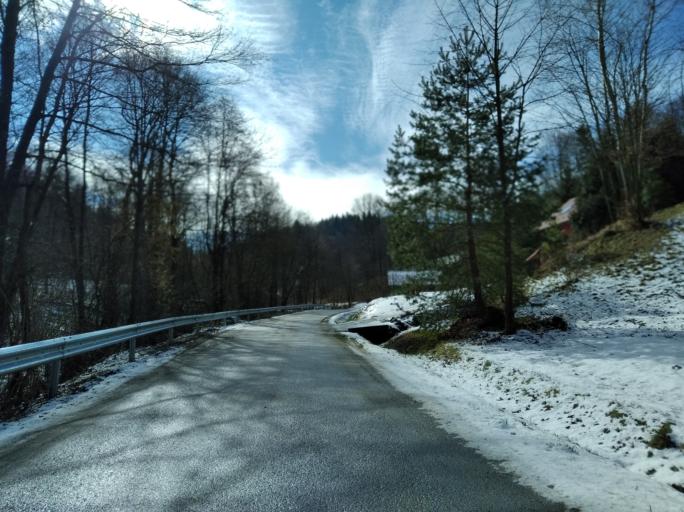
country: PL
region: Subcarpathian Voivodeship
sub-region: Powiat brzozowski
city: Jablonica Polska
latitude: 49.7494
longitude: 21.8806
